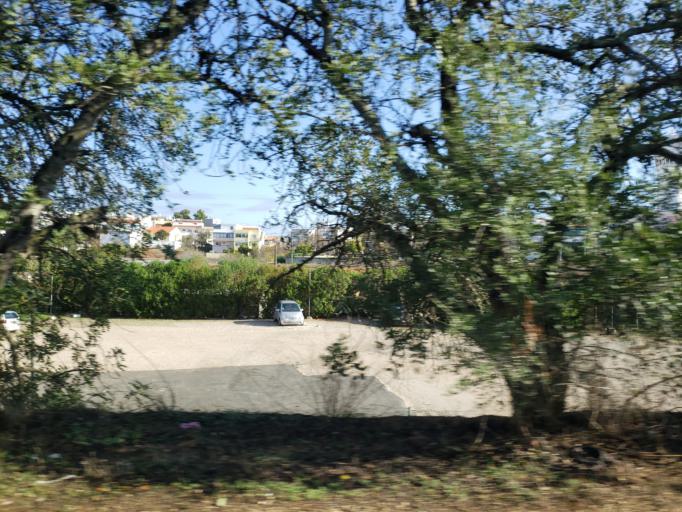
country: PT
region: Faro
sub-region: Portimao
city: Portimao
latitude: 37.1570
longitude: -8.5615
